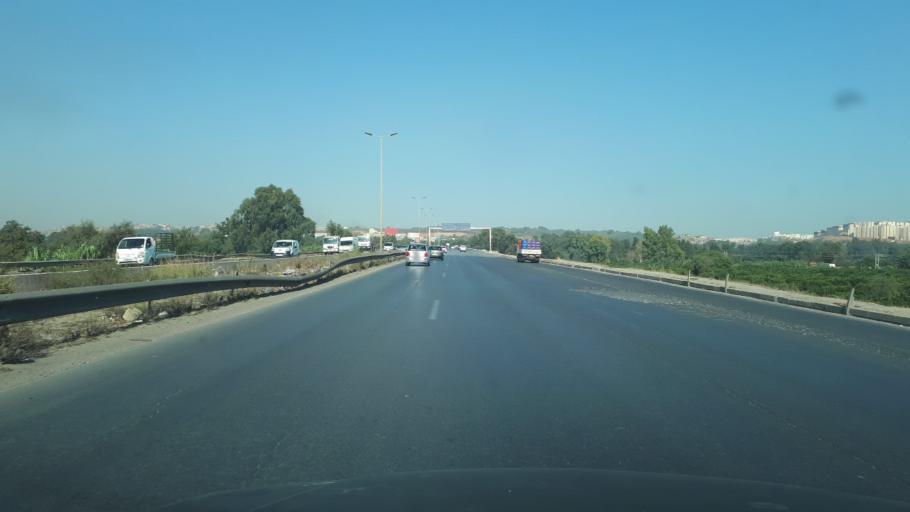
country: DZ
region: Tipaza
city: Baraki
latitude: 36.6771
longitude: 3.0698
